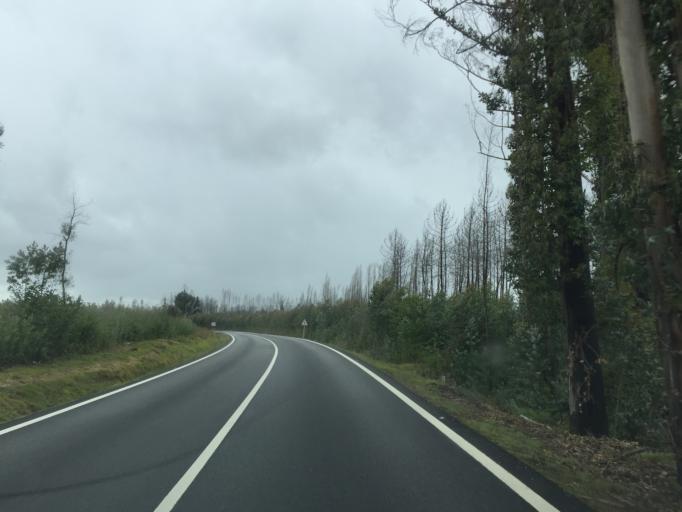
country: PT
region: Coimbra
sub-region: Tabua
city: Tabua
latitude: 40.3278
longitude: -7.9546
